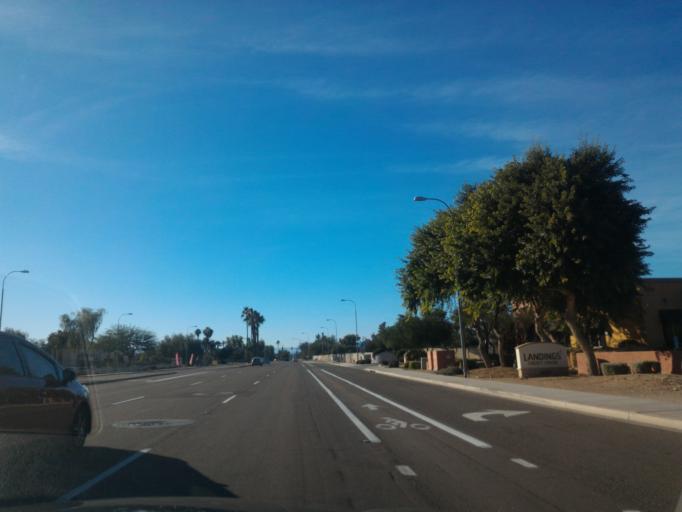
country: US
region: Arizona
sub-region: Maricopa County
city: Guadalupe
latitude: 33.3056
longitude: -111.9256
